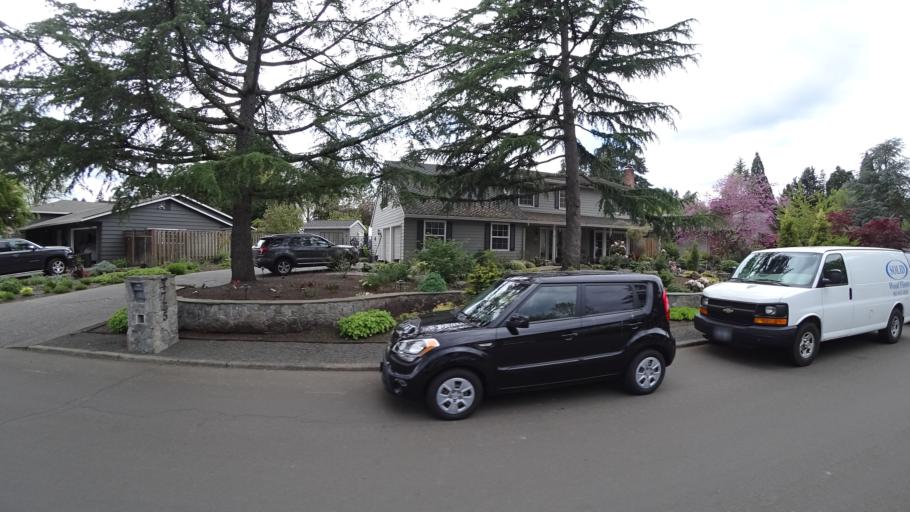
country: US
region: Oregon
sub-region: Washington County
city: Rockcreek
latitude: 45.5535
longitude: -122.8790
